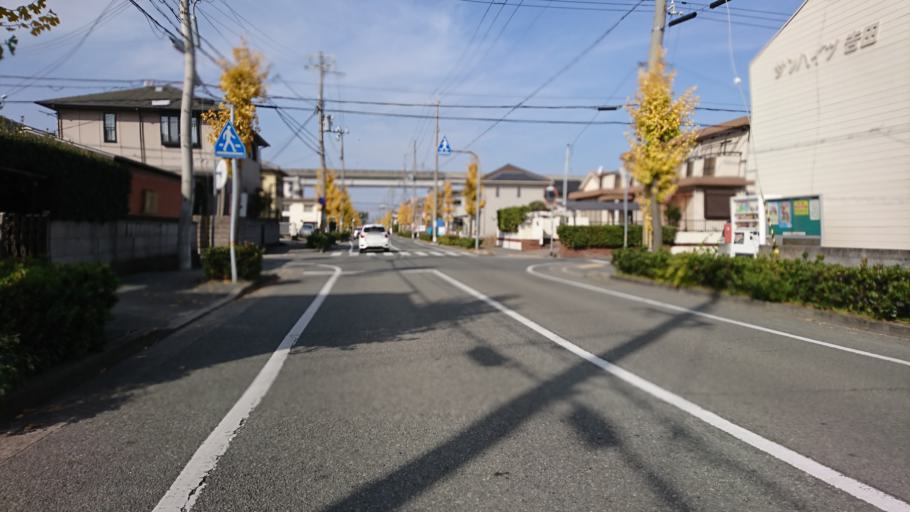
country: JP
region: Hyogo
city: Kakogawacho-honmachi
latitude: 34.7345
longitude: 134.8413
